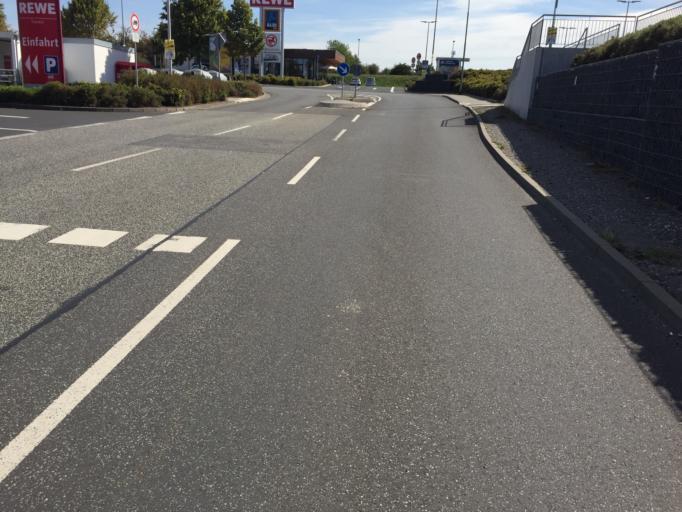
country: DE
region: Hesse
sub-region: Regierungsbezirk Giessen
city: Langgons
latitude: 50.4927
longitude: 8.6555
